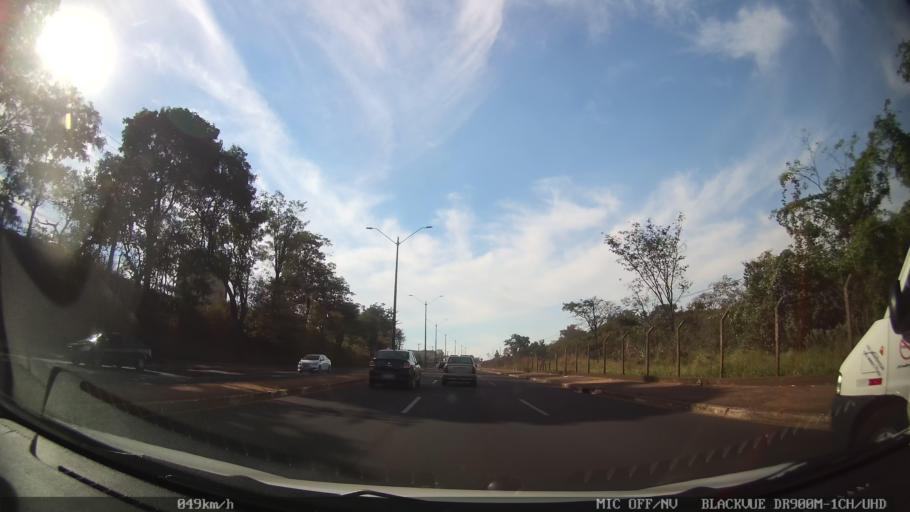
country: BR
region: Sao Paulo
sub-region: Araraquara
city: Araraquara
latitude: -21.7728
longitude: -48.1662
